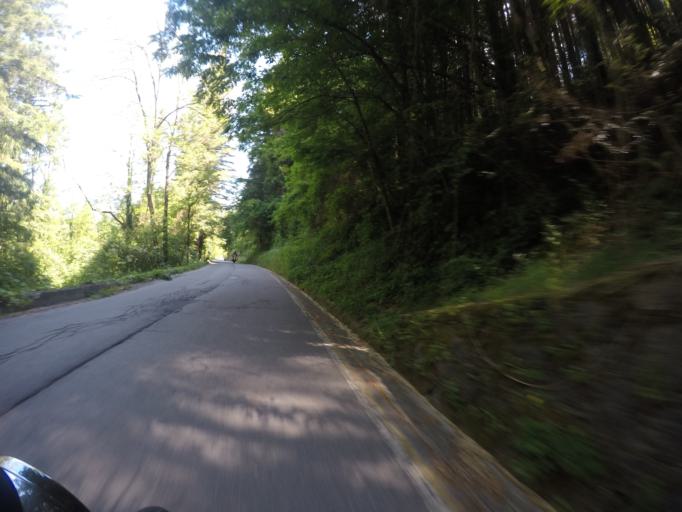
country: IT
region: Tuscany
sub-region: Provincia di Lucca
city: Camporgiano
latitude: 44.1379
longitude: 10.3469
